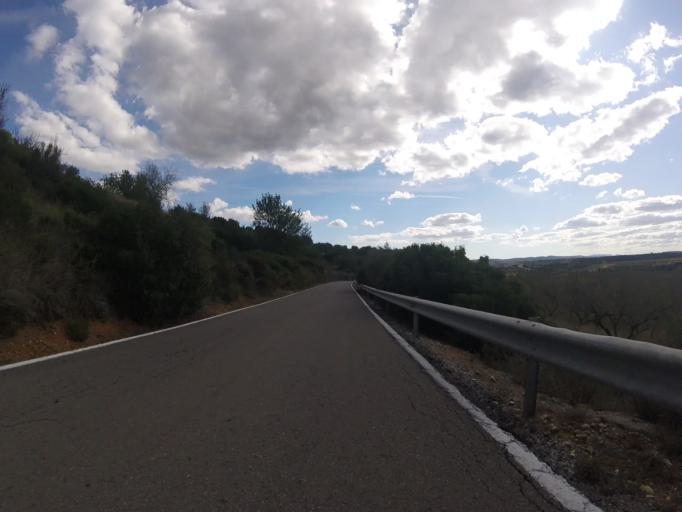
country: ES
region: Valencia
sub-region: Provincia de Castello
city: Cuevas de Vinroma
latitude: 40.3557
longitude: 0.1266
